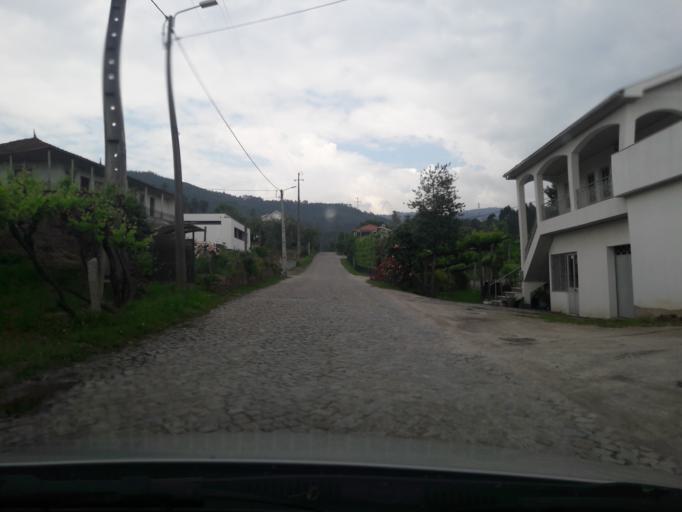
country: PT
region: Porto
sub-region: Amarante
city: Teloes
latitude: 41.3317
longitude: -8.0692
